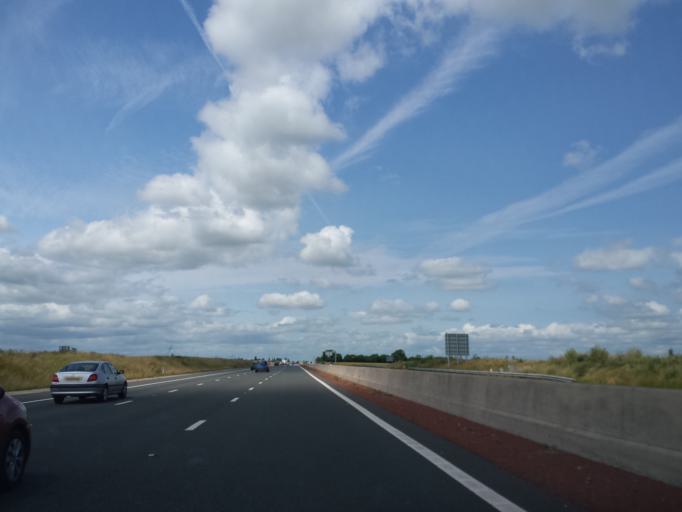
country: GB
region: England
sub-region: North Yorkshire
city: Ripon
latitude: 54.1997
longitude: -1.4701
